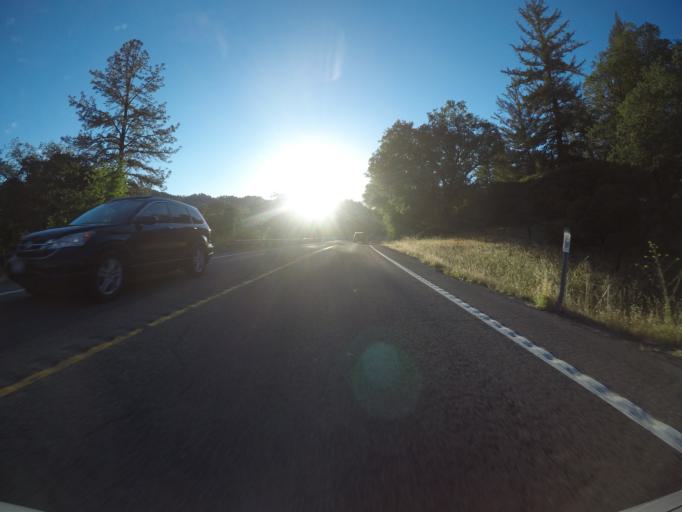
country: US
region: California
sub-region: Mendocino County
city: Laytonville
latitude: 39.7494
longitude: -123.5321
